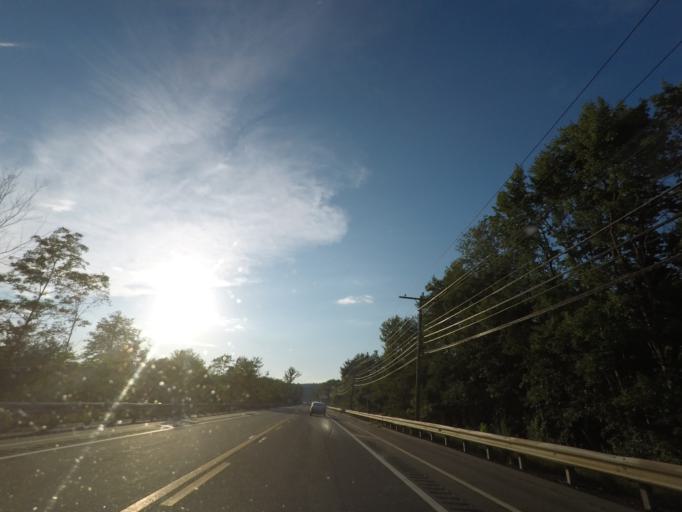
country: US
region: Massachusetts
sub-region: Hampden County
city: Brimfield
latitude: 42.1123
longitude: -72.1829
